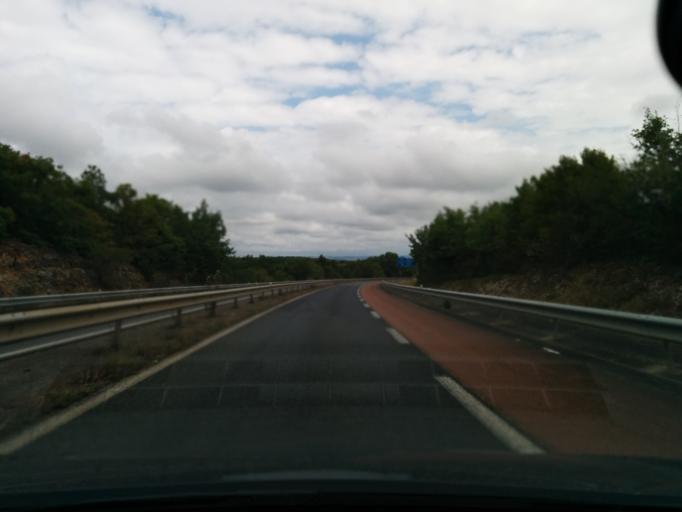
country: FR
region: Limousin
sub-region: Departement de la Correze
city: Brive-la-Gaillarde
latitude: 45.0571
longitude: 1.4986
